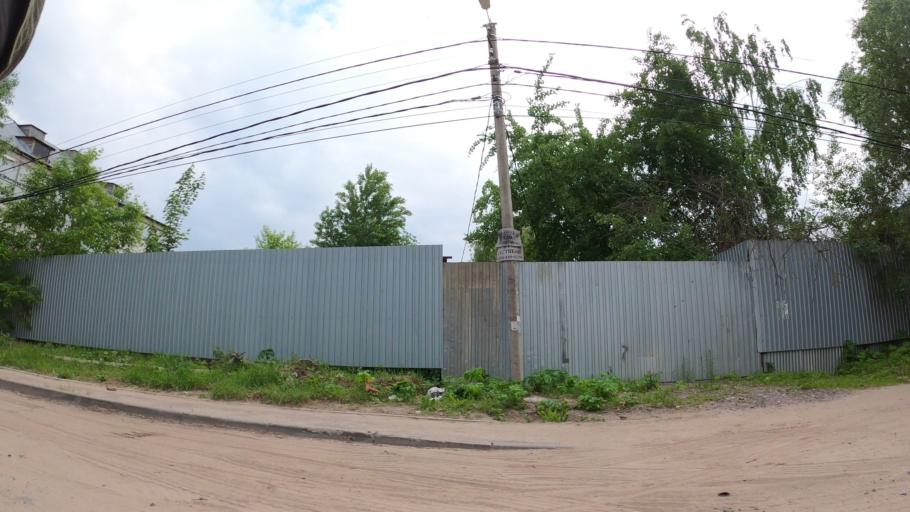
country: RU
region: Moskovskaya
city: Ivanteyevka
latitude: 55.9590
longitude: 37.9230
